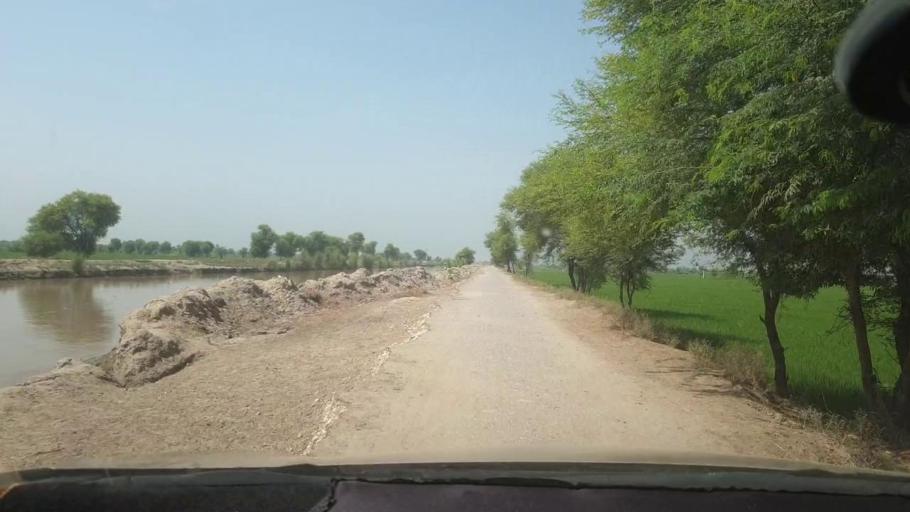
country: PK
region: Sindh
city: Shahdadkot
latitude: 27.7038
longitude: 67.9158
